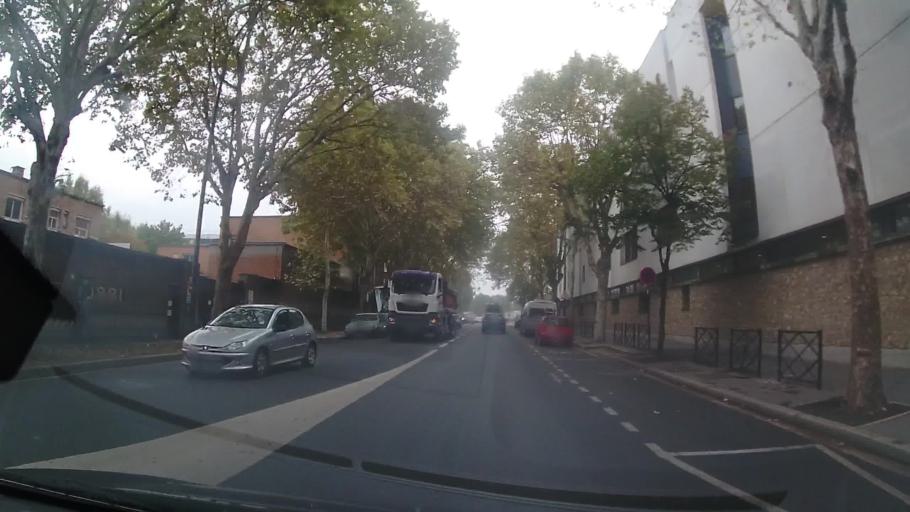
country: FR
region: Ile-de-France
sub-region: Departement des Hauts-de-Seine
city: Clichy
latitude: 48.9078
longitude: 2.3128
